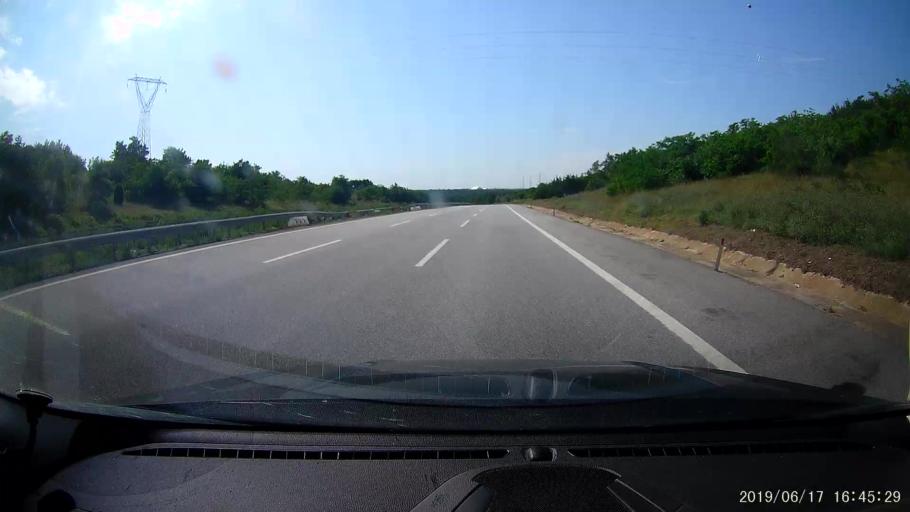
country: TR
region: Kirklareli
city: Babaeski
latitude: 41.4891
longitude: 27.2314
